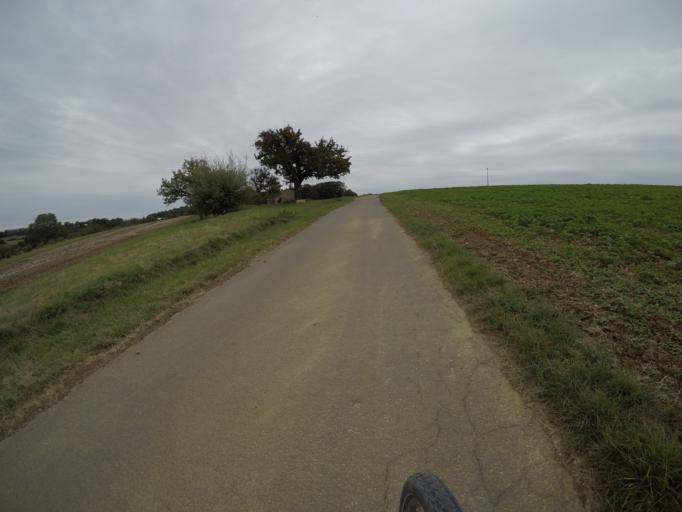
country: DE
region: Baden-Wuerttemberg
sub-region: Regierungsbezirk Stuttgart
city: Eberdingen
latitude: 48.8887
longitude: 8.9770
